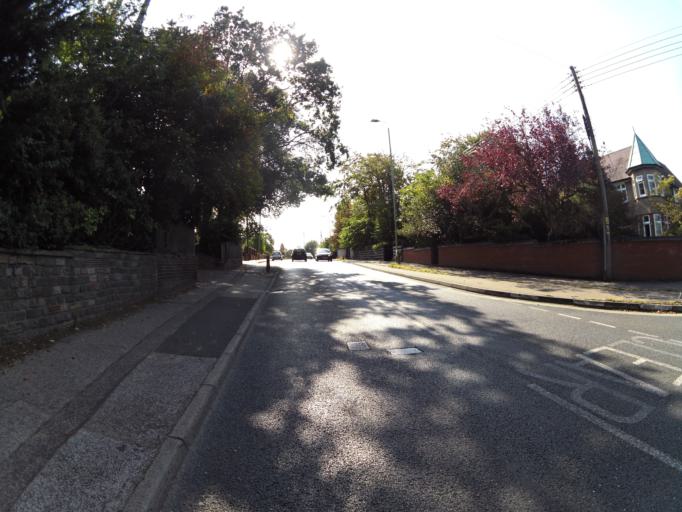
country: GB
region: England
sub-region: Suffolk
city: Lowestoft
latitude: 52.4664
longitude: 1.7085
